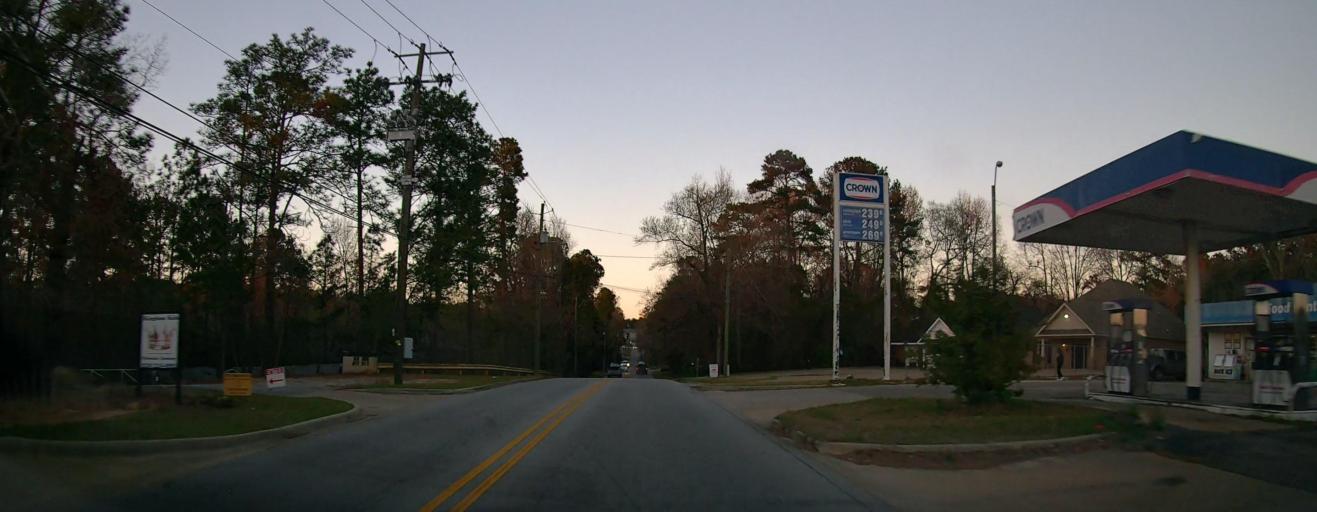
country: US
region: Alabama
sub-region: Russell County
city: Phenix City
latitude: 32.4872
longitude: -85.0207
